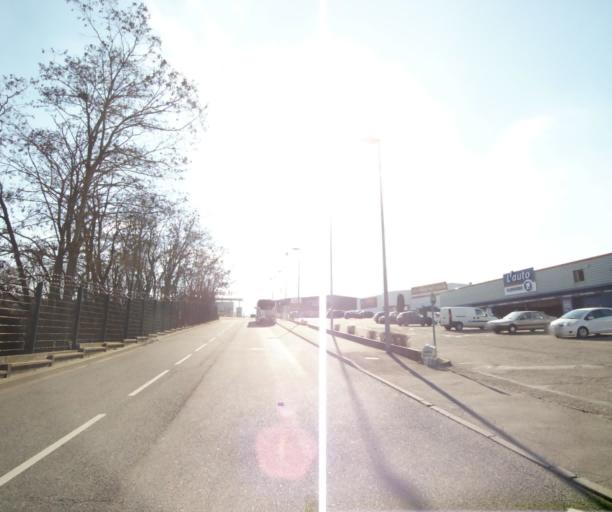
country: FR
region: Lorraine
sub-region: Departement de Meurthe-et-Moselle
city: Vandoeuvre-les-Nancy
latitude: 48.6540
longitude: 6.1800
